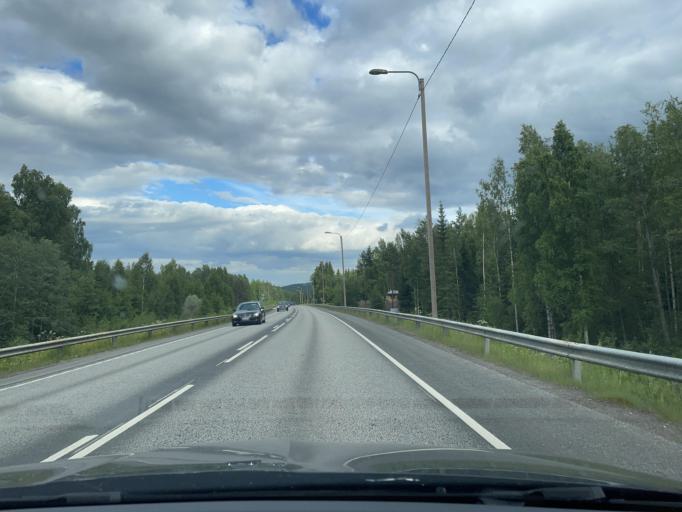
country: FI
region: Central Finland
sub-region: Jyvaeskylae
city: Jyvaeskylae
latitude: 62.2609
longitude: 25.5960
